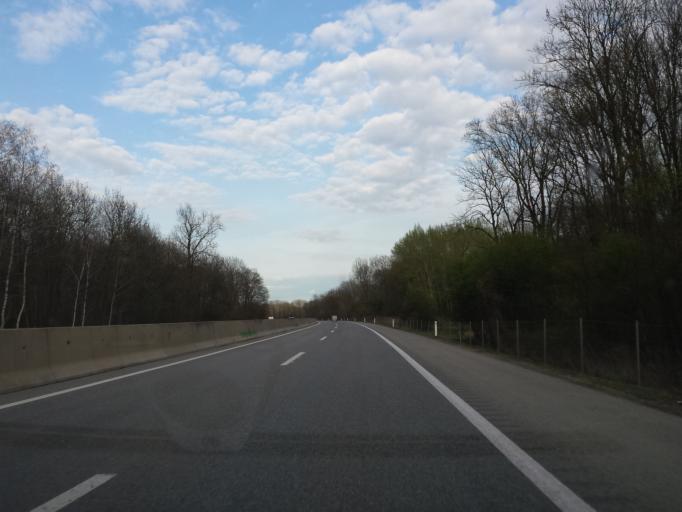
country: AT
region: Lower Austria
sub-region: Politischer Bezirk Korneuburg
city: Hausleiten
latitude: 48.3604
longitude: 16.0821
